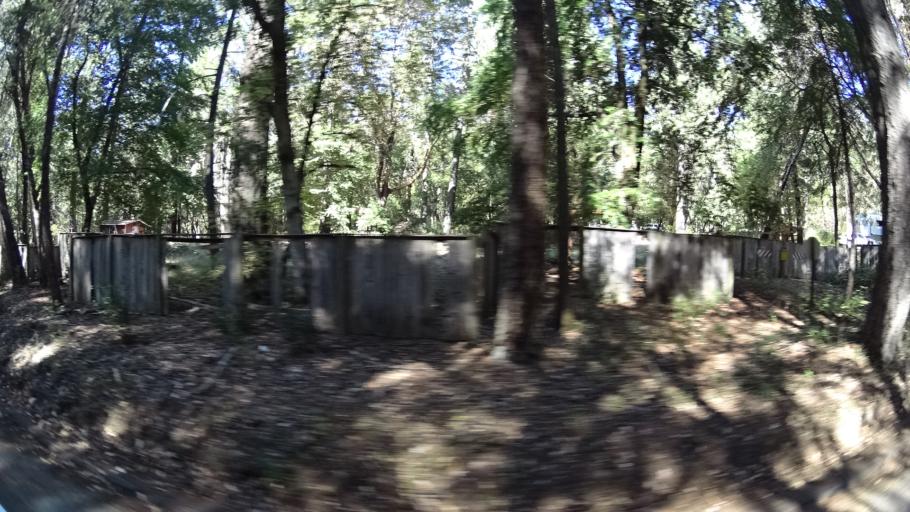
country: US
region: California
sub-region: Siskiyou County
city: Happy Camp
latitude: 41.3757
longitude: -123.4485
